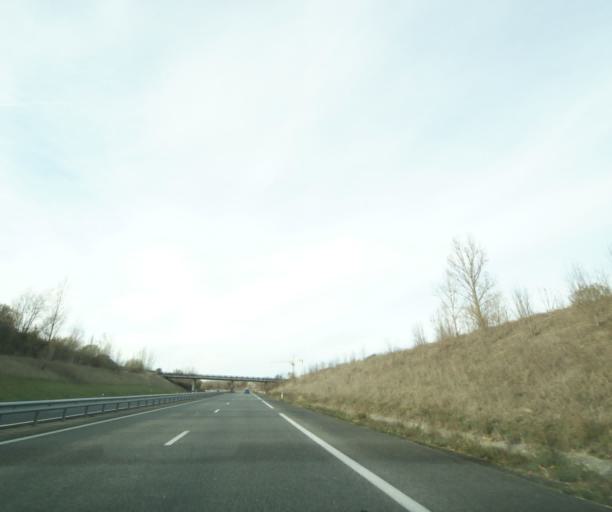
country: FR
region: Midi-Pyrenees
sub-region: Departement du Gers
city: Pujaudran
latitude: 43.6039
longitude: 1.0806
